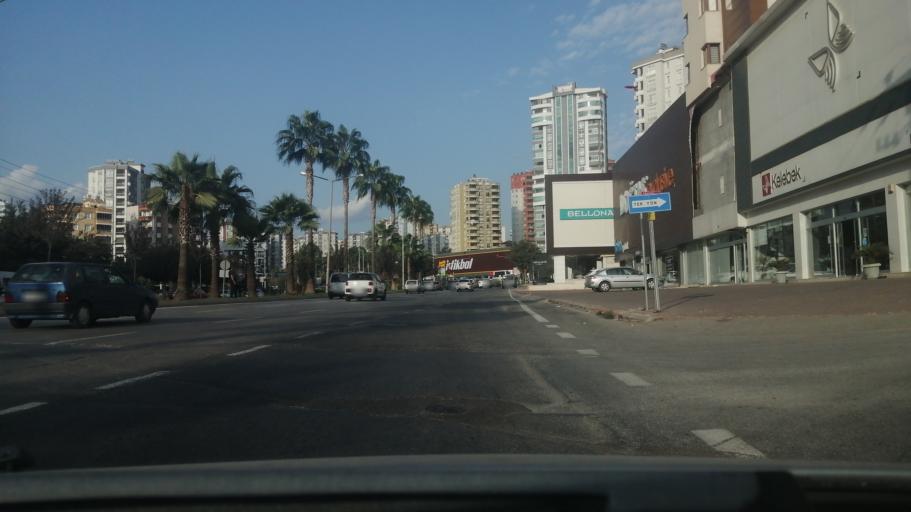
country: TR
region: Adana
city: Seyhan
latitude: 37.0341
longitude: 35.2562
